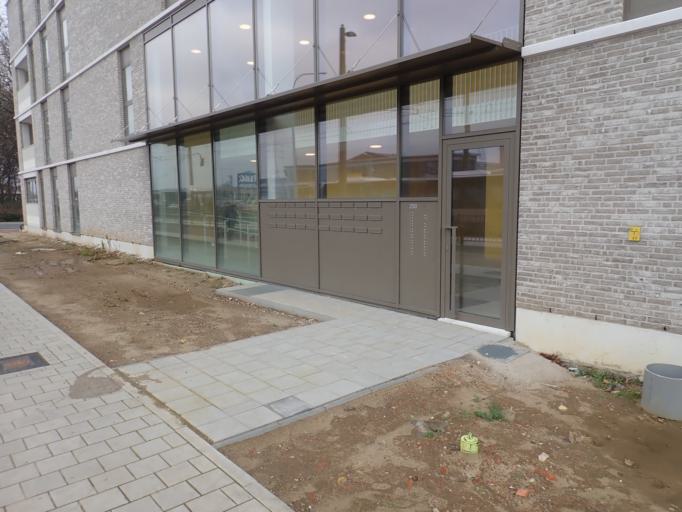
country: BE
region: Flanders
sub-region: Provincie Antwerpen
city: Antwerpen
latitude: 51.2568
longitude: 4.4205
